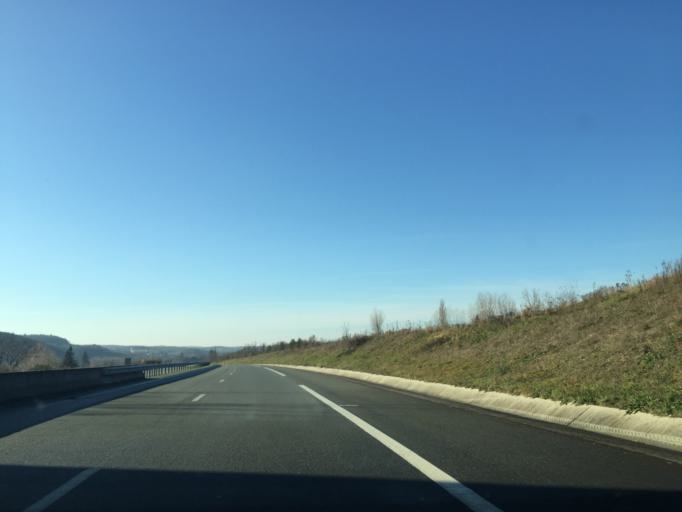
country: FR
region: Aquitaine
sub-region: Departement de la Dordogne
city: Montignac
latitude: 45.1483
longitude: 1.1911
